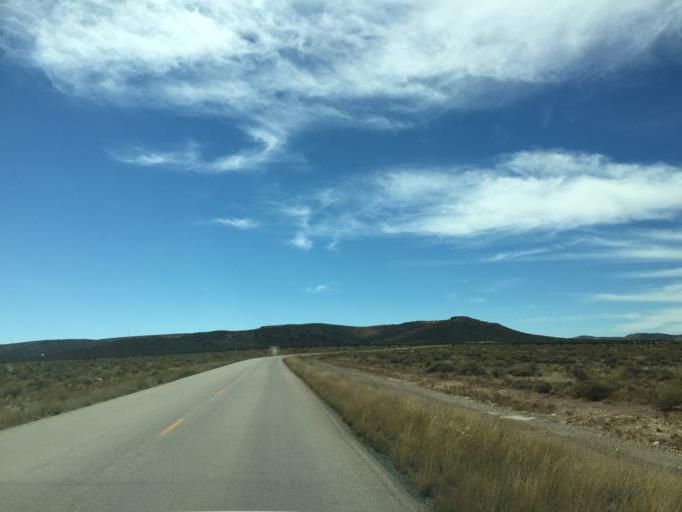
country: US
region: Arizona
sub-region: Mohave County
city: Meadview
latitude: 35.9418
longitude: -113.8627
